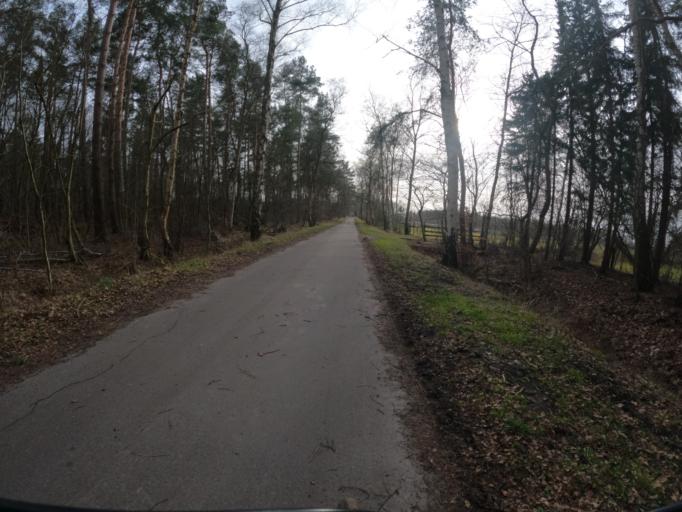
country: DE
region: Schleswig-Holstein
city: Appen
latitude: 53.6111
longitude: 9.7356
